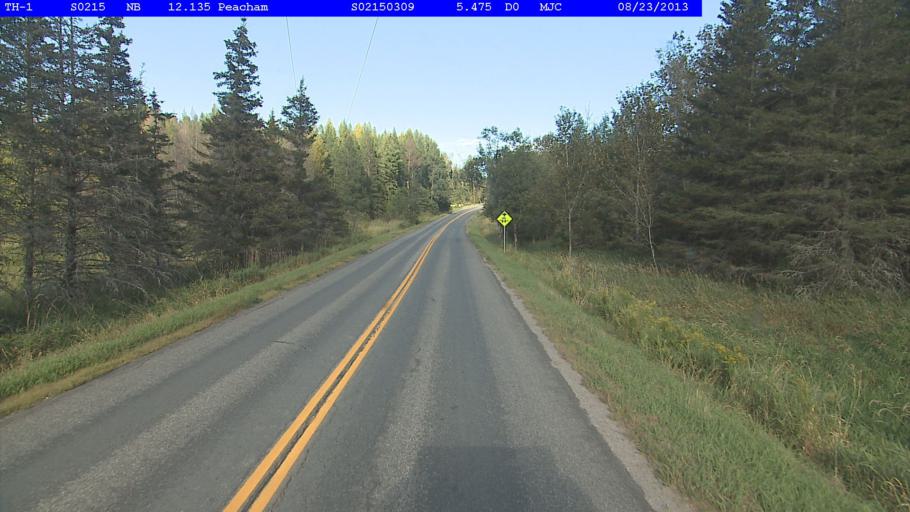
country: US
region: Vermont
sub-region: Caledonia County
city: Saint Johnsbury
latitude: 44.3667
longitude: -72.1555
